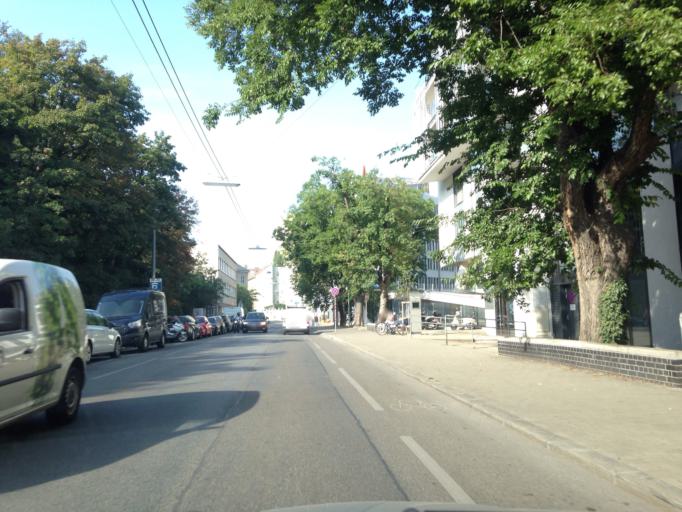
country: AT
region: Vienna
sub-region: Wien Stadt
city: Vienna
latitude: 48.2198
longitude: 16.3540
